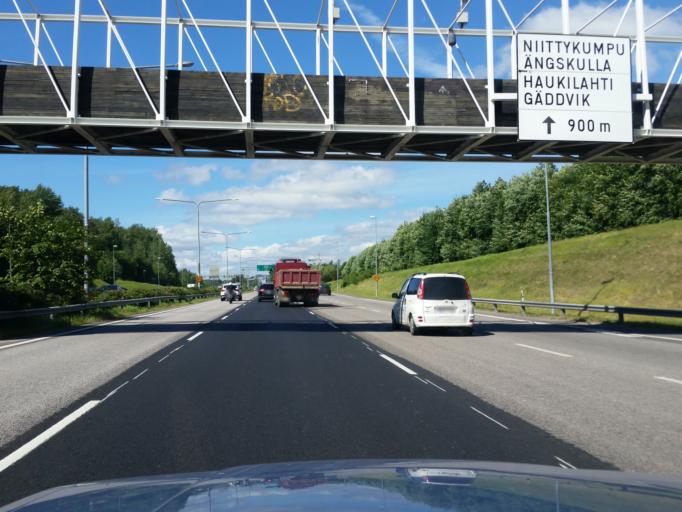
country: FI
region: Uusimaa
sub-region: Helsinki
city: Koukkuniemi
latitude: 60.1687
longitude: 24.7894
